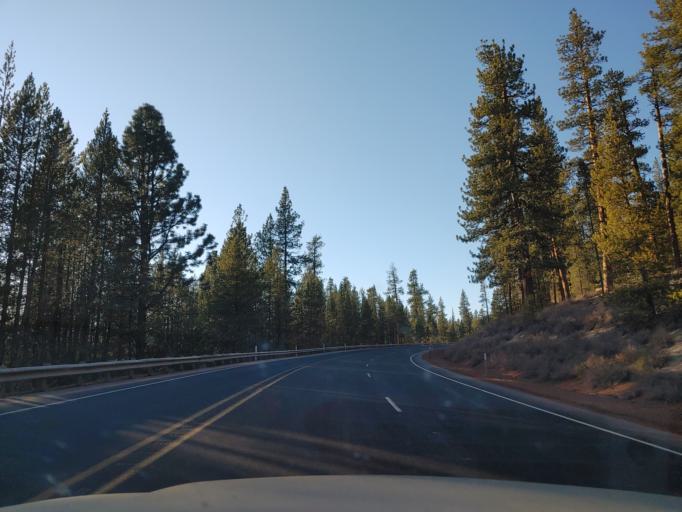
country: US
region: Oregon
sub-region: Deschutes County
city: La Pine
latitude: 43.4435
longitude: -121.8689
